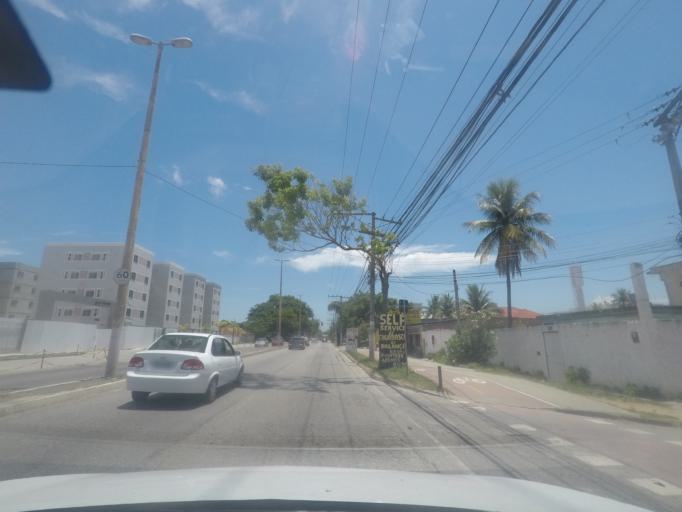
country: BR
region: Rio de Janeiro
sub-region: Itaguai
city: Itaguai
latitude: -22.8979
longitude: -43.6784
